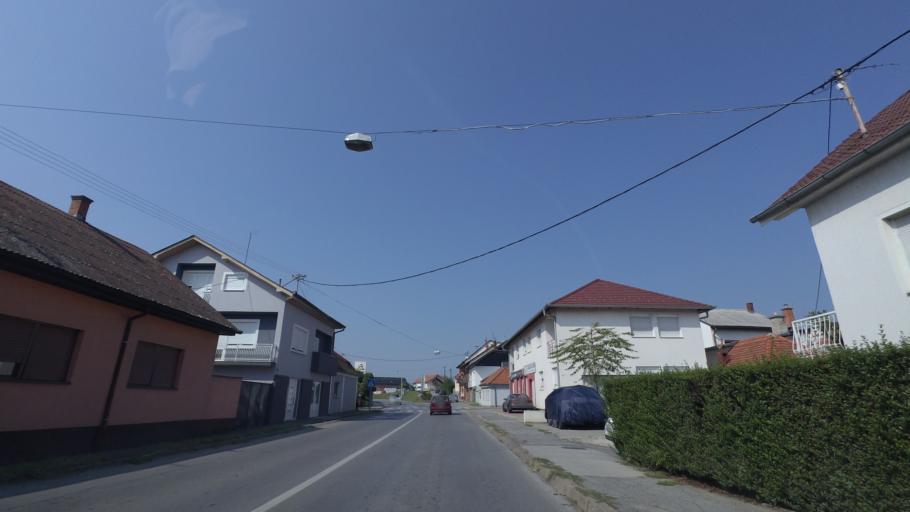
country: HR
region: Pozesko-Slavonska
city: Pozega
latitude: 45.3402
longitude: 17.6730
